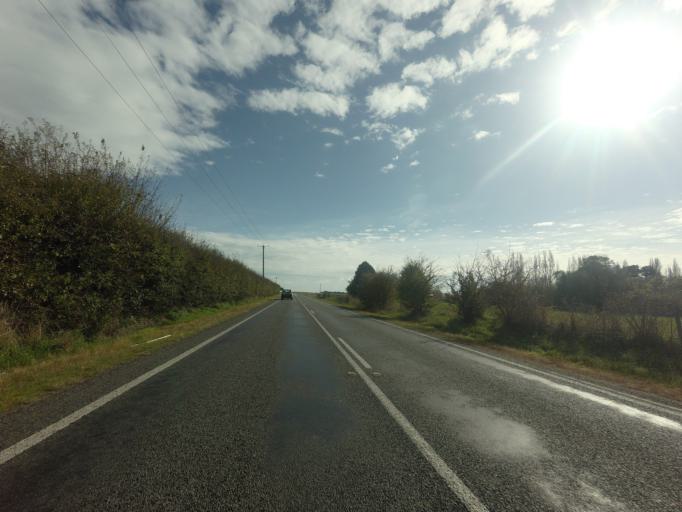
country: AU
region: Tasmania
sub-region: Meander Valley
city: Westbury
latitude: -41.5232
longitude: 146.7799
